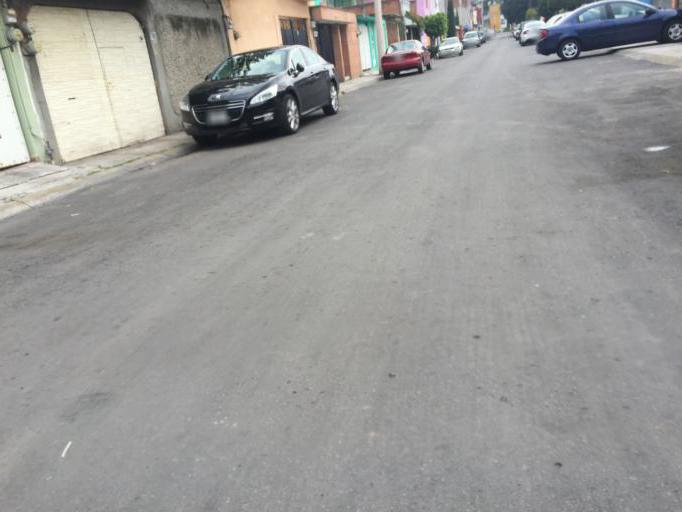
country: MX
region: Mexico
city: Cuautitlan Izcalli
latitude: 19.6583
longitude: -99.2148
